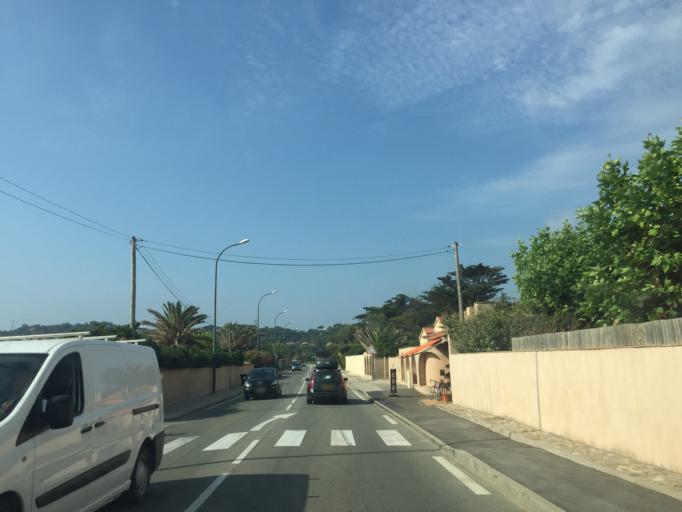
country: FR
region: Provence-Alpes-Cote d'Azur
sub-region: Departement du Var
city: Sainte-Maxime
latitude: 43.3250
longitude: 6.6648
